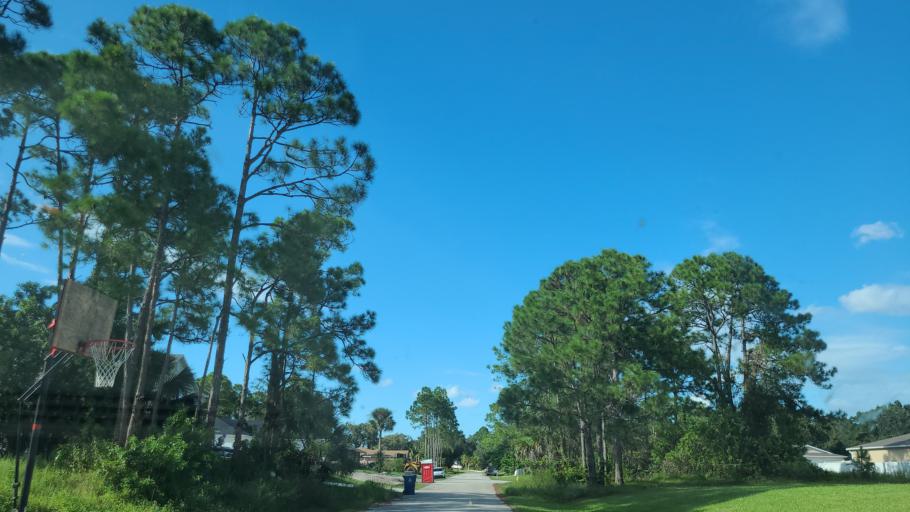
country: US
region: Florida
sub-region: Brevard County
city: June Park
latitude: 27.9814
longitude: -80.6710
